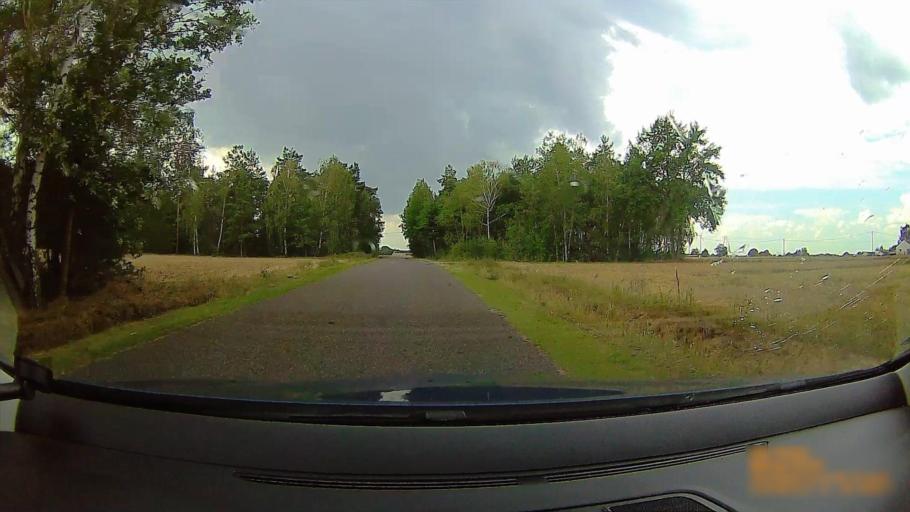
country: PL
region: Greater Poland Voivodeship
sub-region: Powiat koninski
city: Rychwal
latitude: 52.1034
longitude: 18.1742
